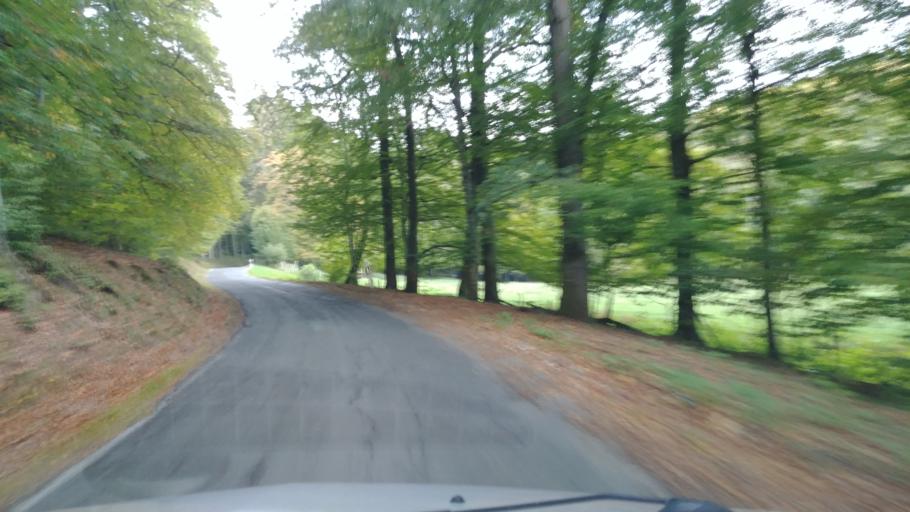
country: DE
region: Rheinland-Pfalz
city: Merschbach
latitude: 49.8117
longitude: 7.0094
